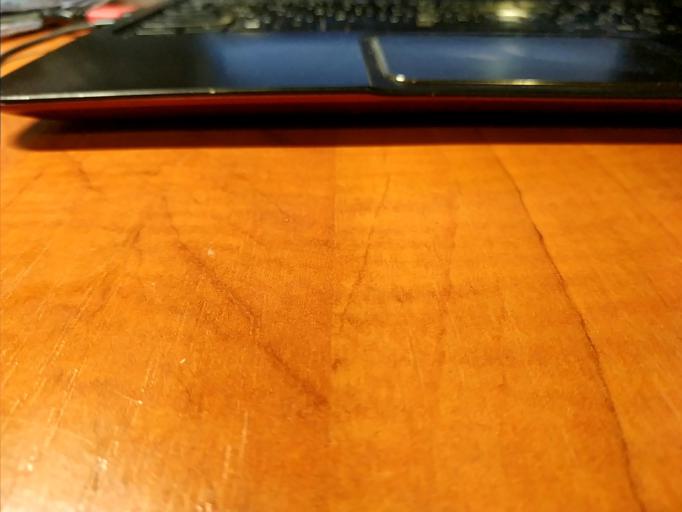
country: RU
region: Tverskaya
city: Ves'yegonsk
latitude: 58.7903
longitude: 37.5442
